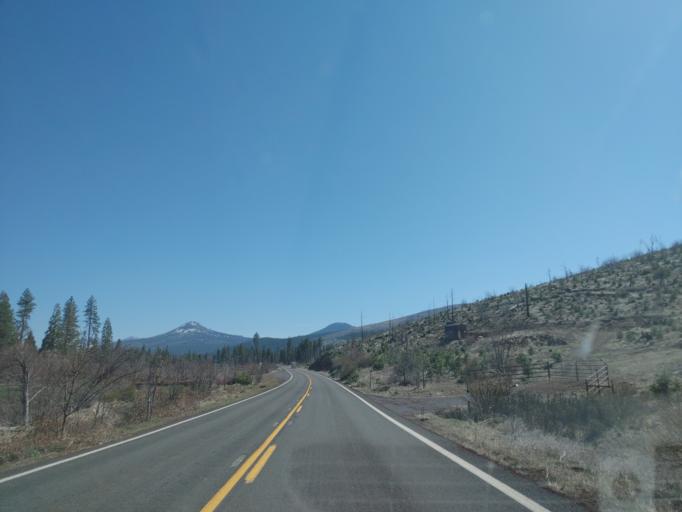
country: US
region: California
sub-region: Shasta County
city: Burney
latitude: 40.7906
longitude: -121.5065
